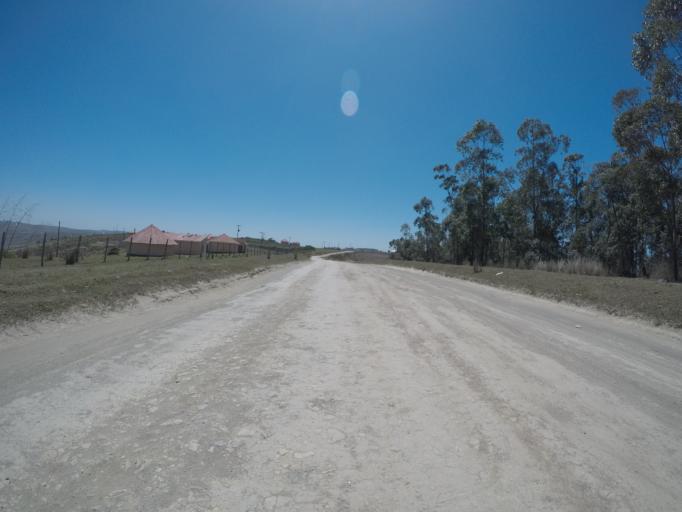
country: ZA
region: Eastern Cape
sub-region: OR Tambo District Municipality
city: Libode
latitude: -31.9488
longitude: 29.0251
